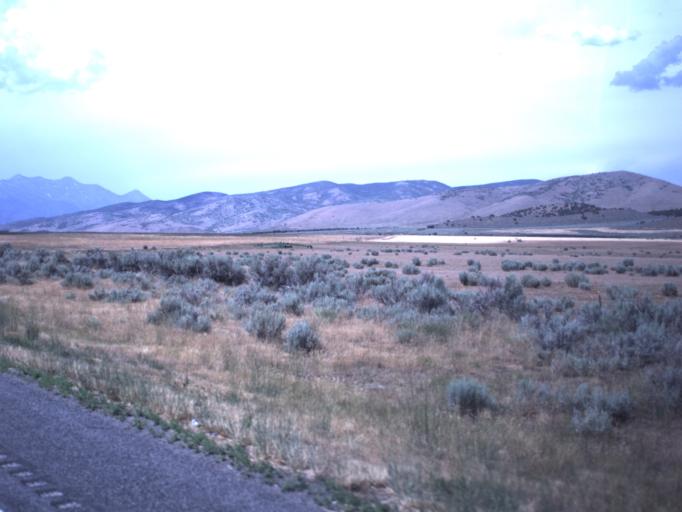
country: US
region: Utah
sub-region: Sanpete County
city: Fountain Green
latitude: 39.6478
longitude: -111.6444
